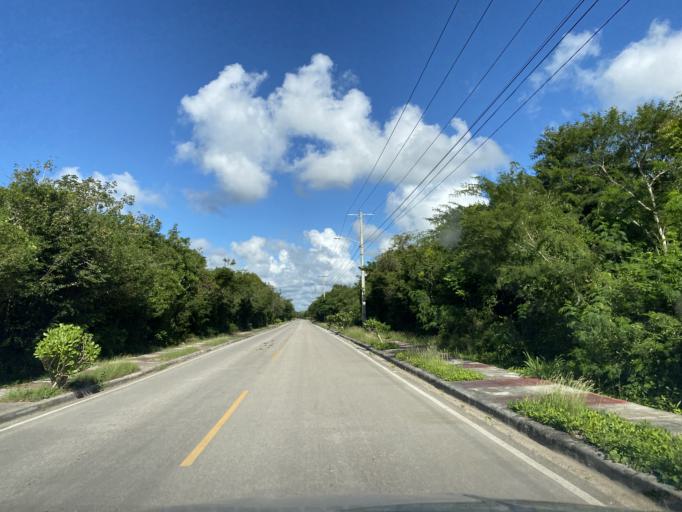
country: DO
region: La Altagracia
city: San Rafael del Yuma
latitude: 18.3352
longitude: -68.8092
